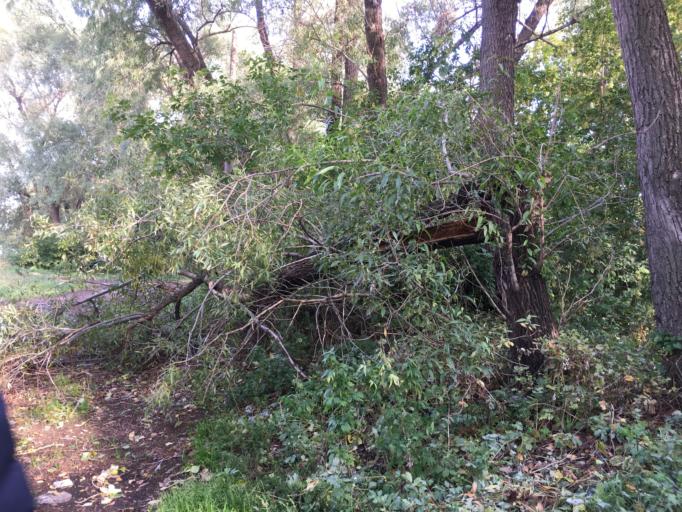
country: RU
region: Bashkortostan
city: Meleuz
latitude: 52.9598
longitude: 55.9272
